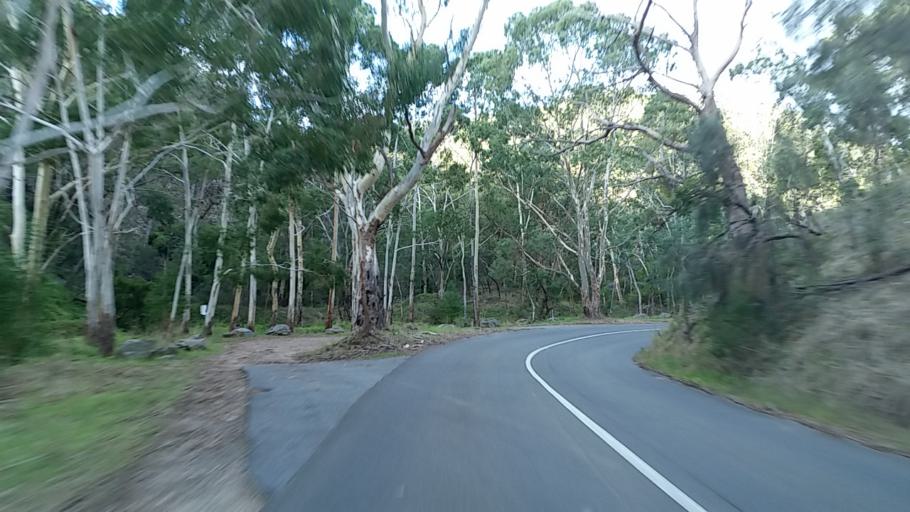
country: AU
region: South Australia
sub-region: Adelaide Hills
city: Adelaide Hills
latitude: -34.8894
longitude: 138.7237
